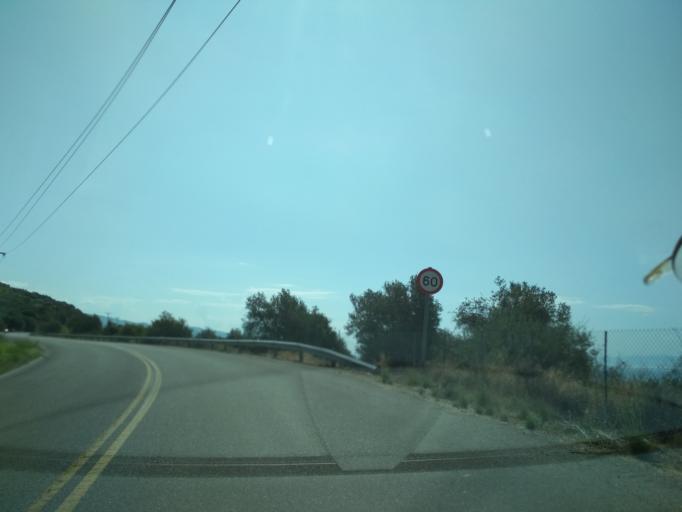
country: GR
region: Central Greece
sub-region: Nomos Evvoias
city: Roviai
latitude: 38.8396
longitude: 23.1756
